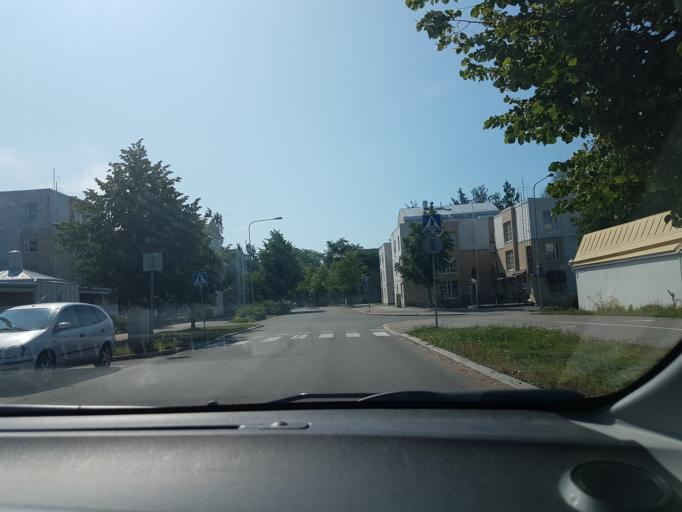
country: FI
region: Uusimaa
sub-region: Helsinki
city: Vantaa
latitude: 60.2040
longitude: 25.1271
